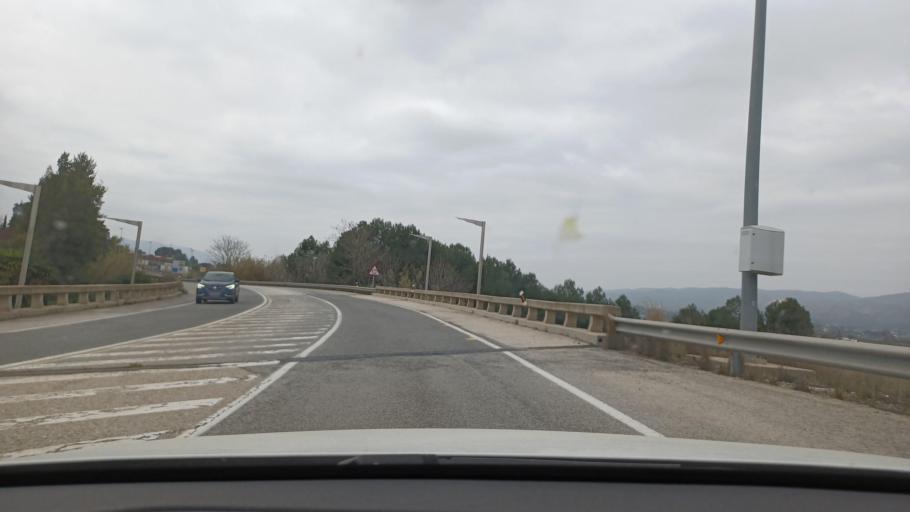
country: ES
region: Valencia
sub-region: Provincia de Valencia
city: Agullent
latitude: 38.8342
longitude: -0.5634
